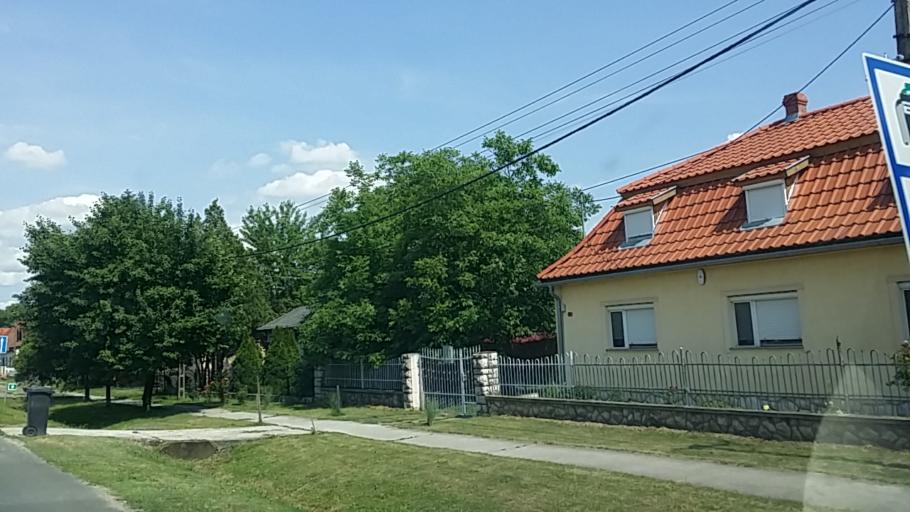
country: HU
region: Baranya
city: Harkany
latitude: 45.8467
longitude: 18.2354
